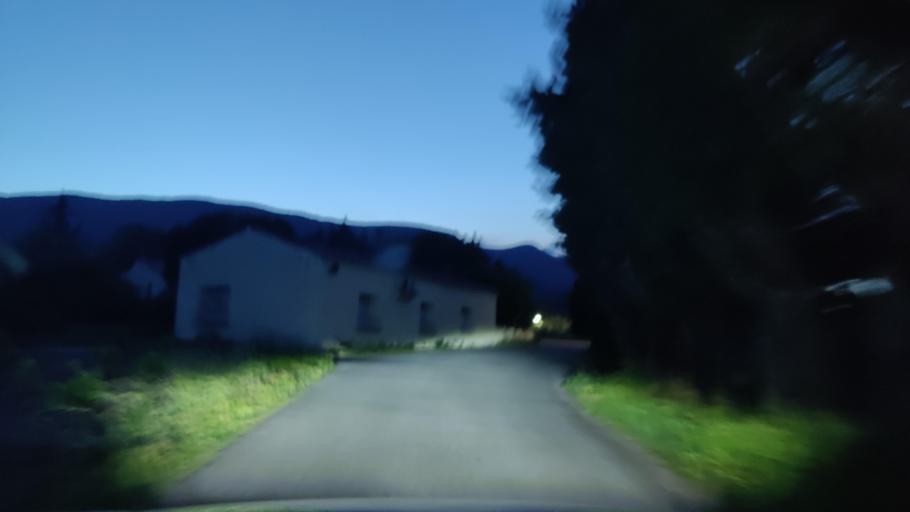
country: FR
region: Languedoc-Roussillon
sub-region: Departement des Pyrenees-Orientales
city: Estagel
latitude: 42.8865
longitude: 2.7264
